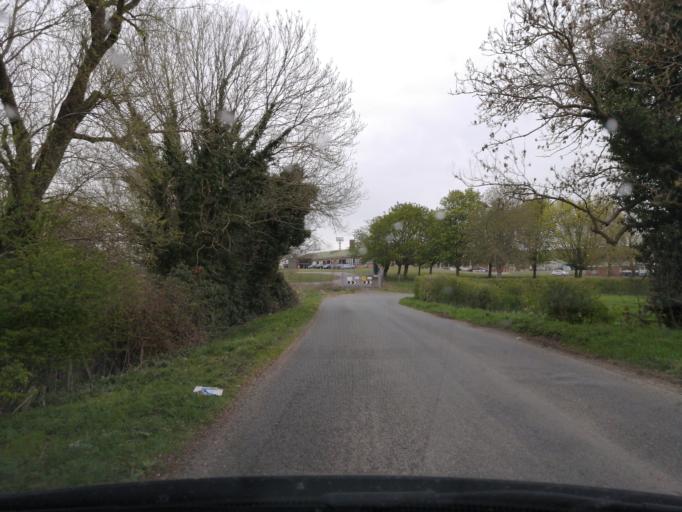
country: GB
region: England
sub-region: Peterborough
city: Wittering
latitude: 52.6093
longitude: -0.4611
